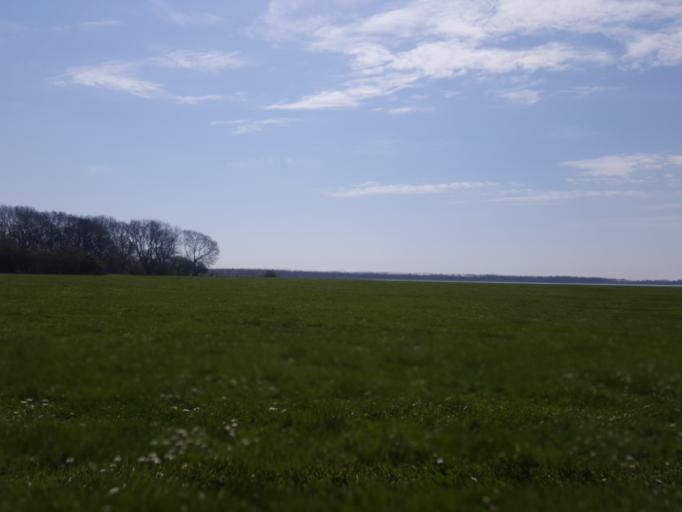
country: DK
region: Capital Region
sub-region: Frederiksberg Kommune
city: Frederiksberg
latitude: 55.6391
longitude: 12.5240
